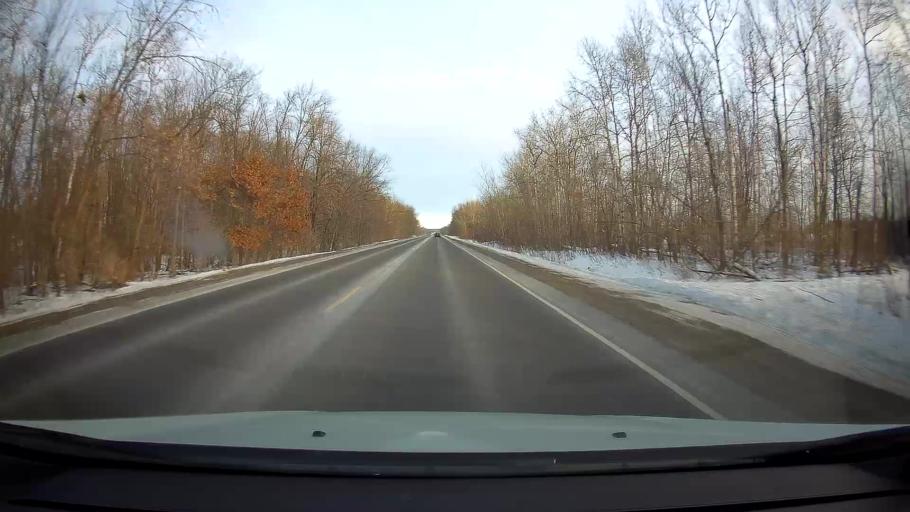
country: US
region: Wisconsin
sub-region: Polk County
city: Clear Lake
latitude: 45.2907
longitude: -92.2301
